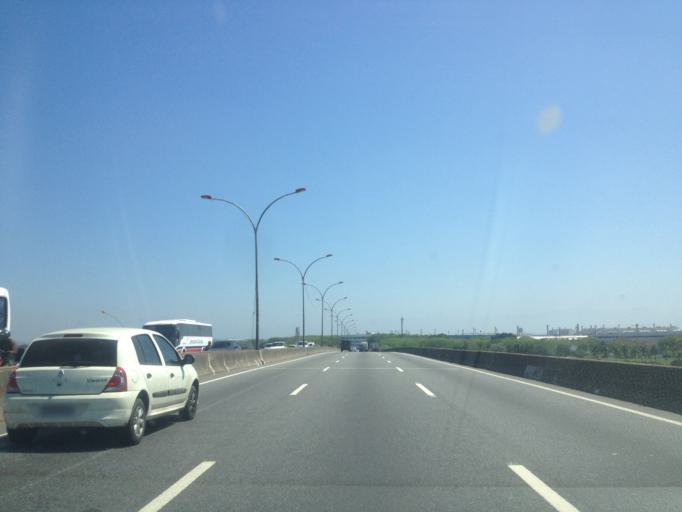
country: BR
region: Rio de Janeiro
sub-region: Rio De Janeiro
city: Rio de Janeiro
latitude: -22.8355
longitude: -43.2447
